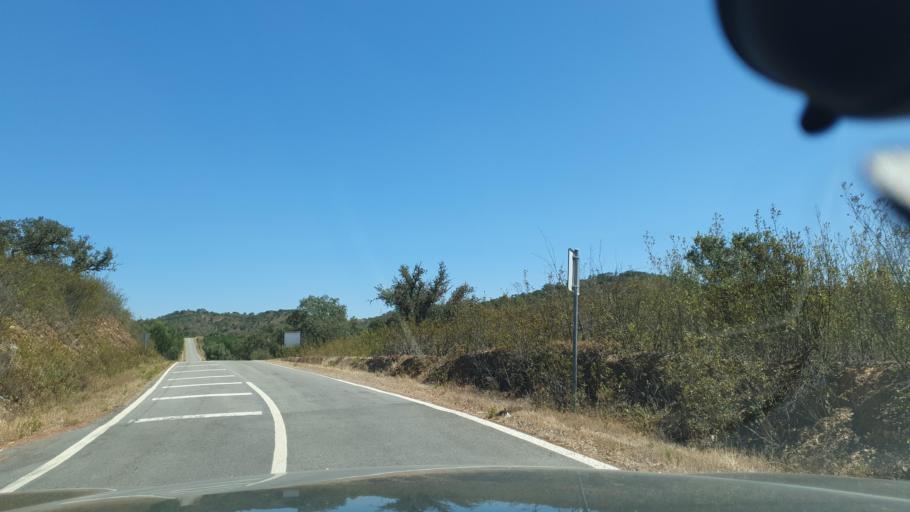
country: PT
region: Beja
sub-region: Odemira
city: Odemira
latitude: 37.5190
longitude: -8.4750
